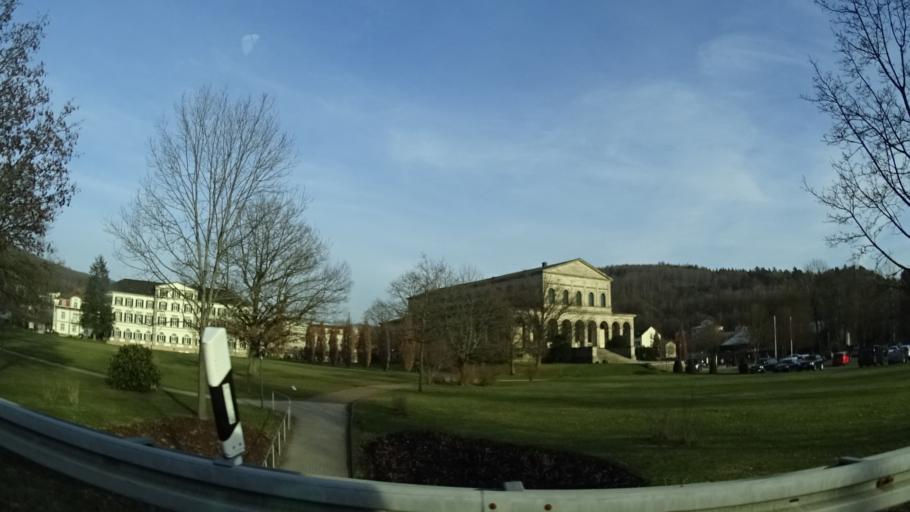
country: DE
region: Bavaria
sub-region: Regierungsbezirk Unterfranken
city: Bad Bruckenau
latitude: 50.3031
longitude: 9.7453
